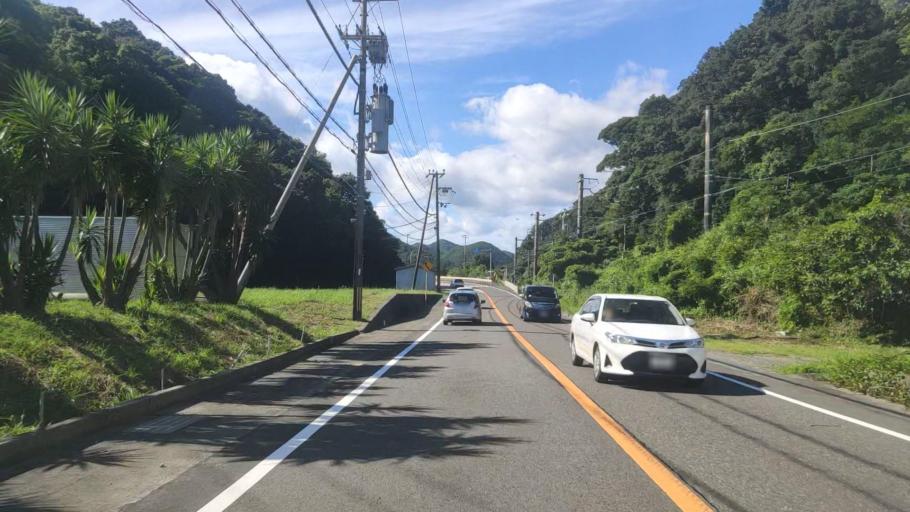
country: JP
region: Wakayama
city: Shingu
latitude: 33.4808
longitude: 135.7701
